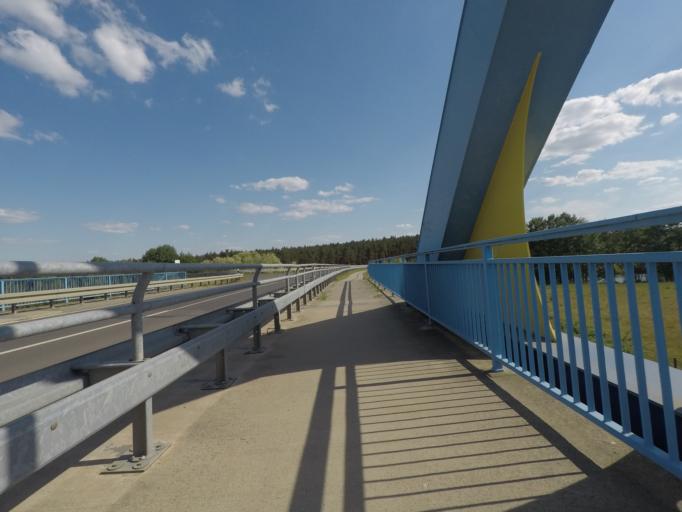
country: DE
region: Brandenburg
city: Eberswalde
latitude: 52.8538
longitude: 13.7984
